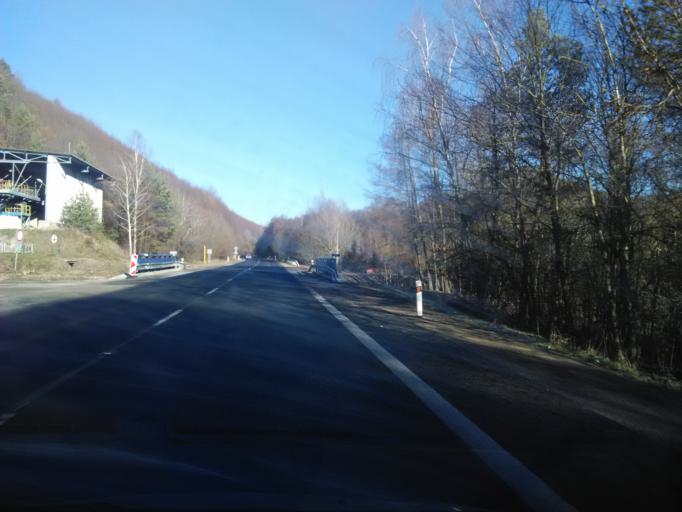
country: SK
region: Banskobystricky
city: Ziar nad Hronom
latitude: 48.6232
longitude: 18.8970
